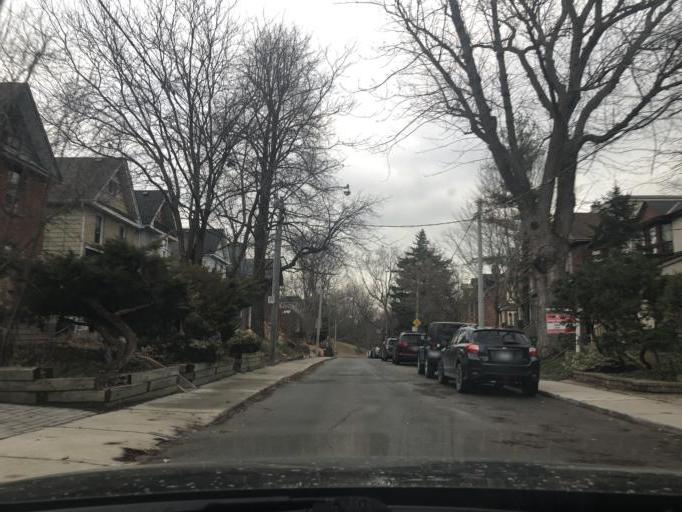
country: CA
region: Ontario
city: Toronto
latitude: 43.6738
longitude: -79.3496
